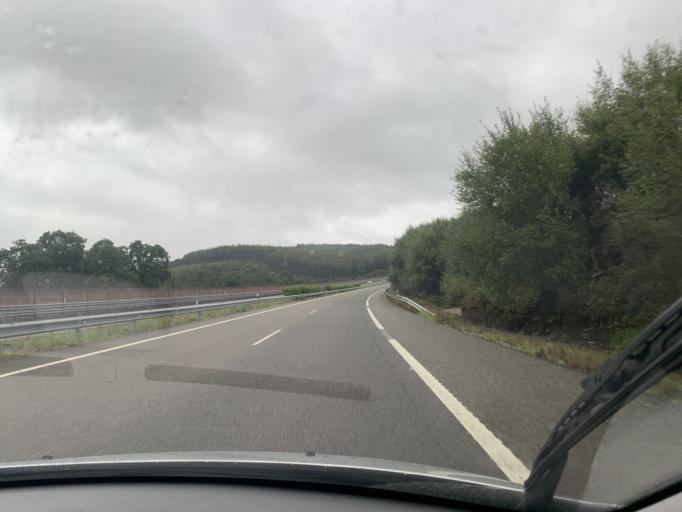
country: ES
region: Galicia
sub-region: Provincia de Lugo
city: Abadin
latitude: 43.3505
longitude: -7.5007
